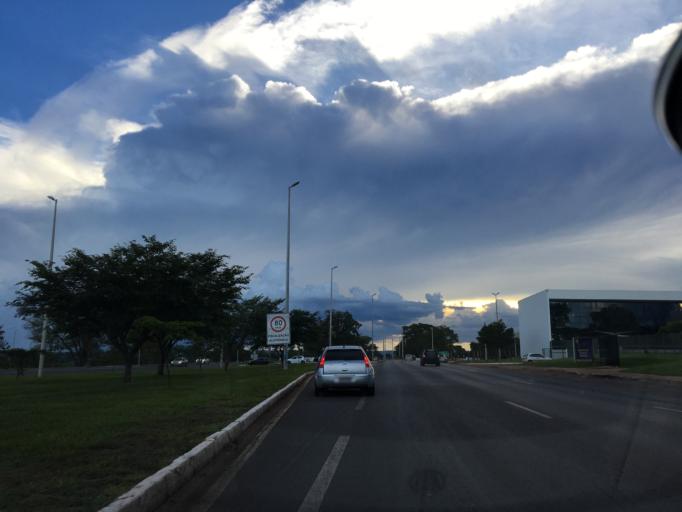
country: BR
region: Federal District
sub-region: Brasilia
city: Brasilia
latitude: -15.8085
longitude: -47.8592
